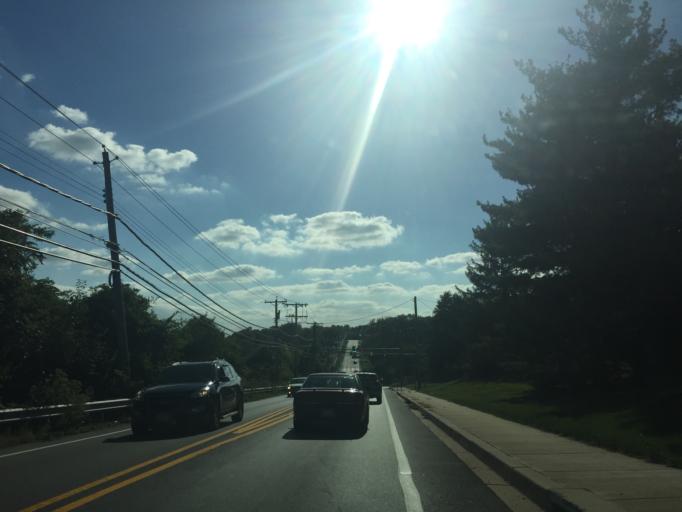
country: US
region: Maryland
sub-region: Baltimore County
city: Rossville
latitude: 39.3469
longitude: -76.4733
